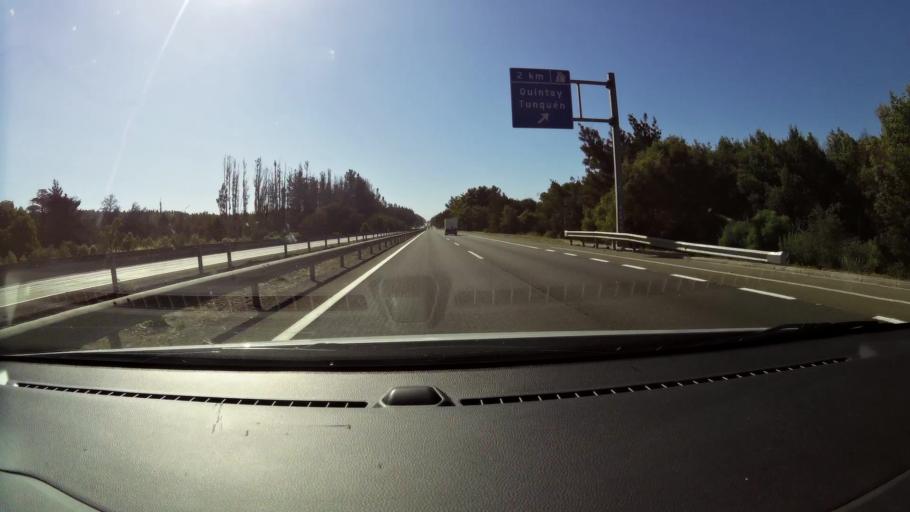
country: CL
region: Valparaiso
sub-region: Provincia de Marga Marga
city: Quilpue
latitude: -33.1738
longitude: -71.5173
